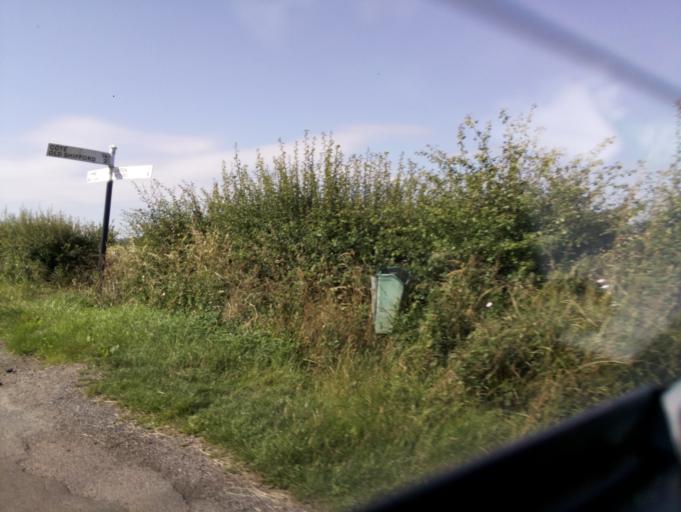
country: GB
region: England
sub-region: Oxfordshire
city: Ducklington
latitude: 51.7199
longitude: -1.4953
